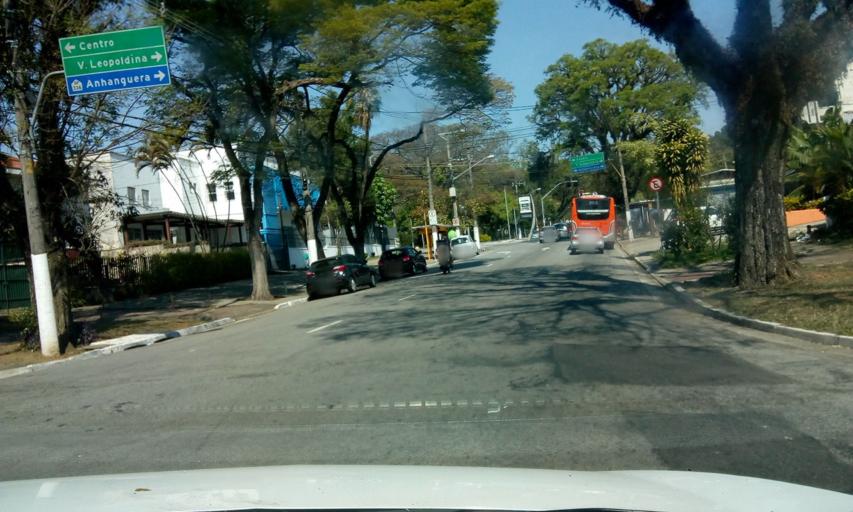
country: BR
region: Sao Paulo
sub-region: Osasco
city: Osasco
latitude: -23.5249
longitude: -46.7136
